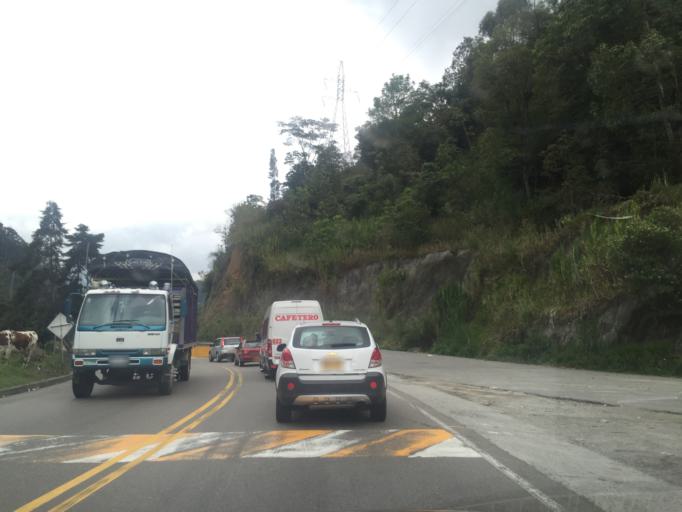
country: CO
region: Tolima
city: Cajamarca
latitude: 4.4354
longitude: -75.4465
